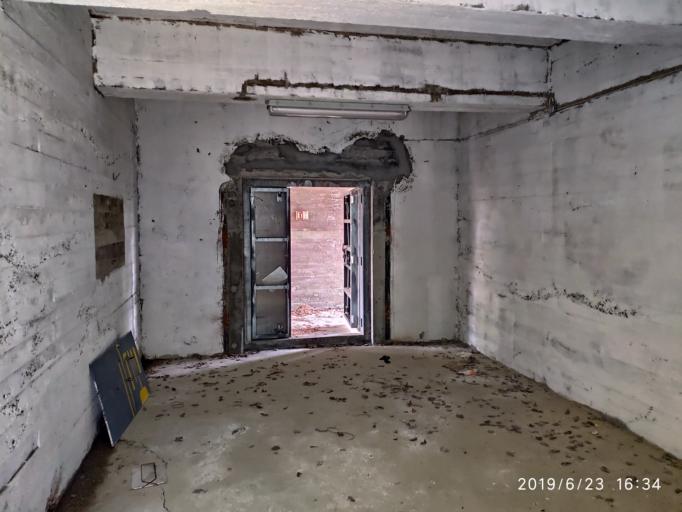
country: NO
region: Buskerud
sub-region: Ringerike
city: Honefoss
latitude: 60.1942
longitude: 10.2944
